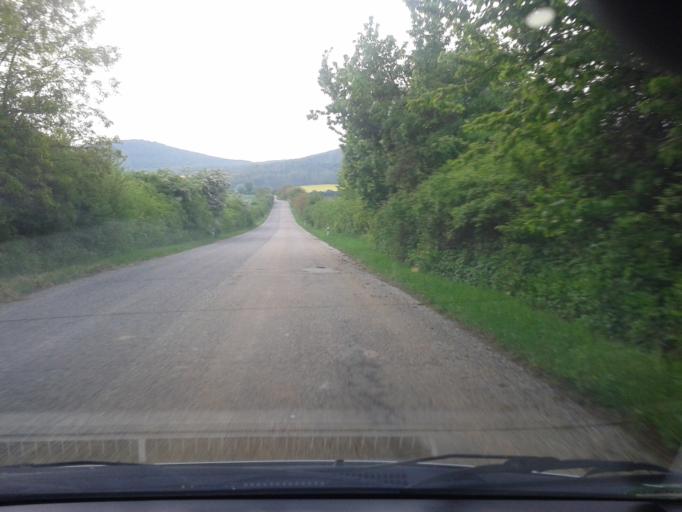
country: SK
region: Nitriansky
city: Tlmace
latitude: 48.2876
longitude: 18.4581
